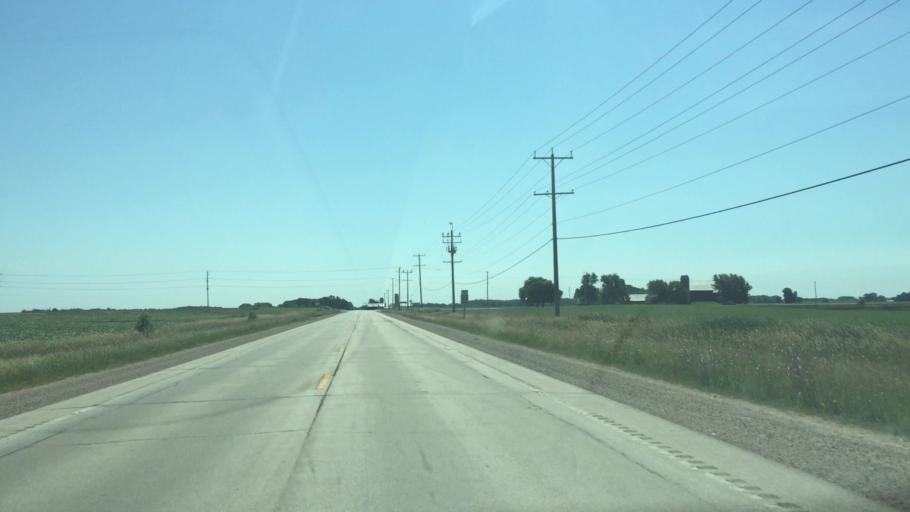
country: US
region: Wisconsin
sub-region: Calumet County
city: Hilbert
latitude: 44.1404
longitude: -88.2091
